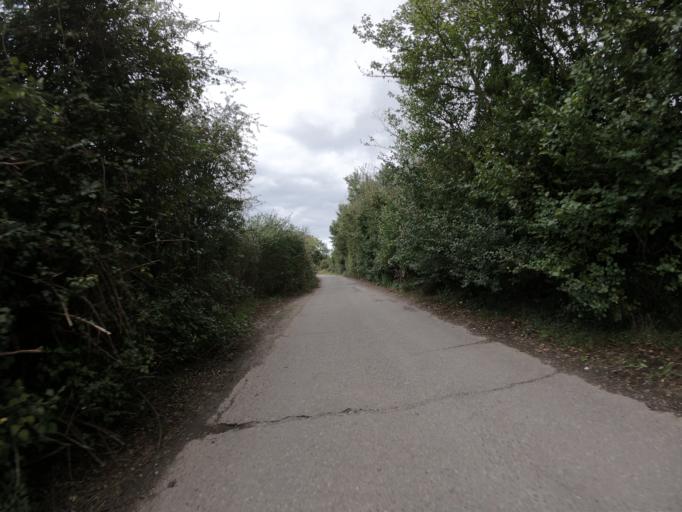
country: GB
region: England
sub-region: Kent
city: Dartford
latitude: 51.4664
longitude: 0.2163
